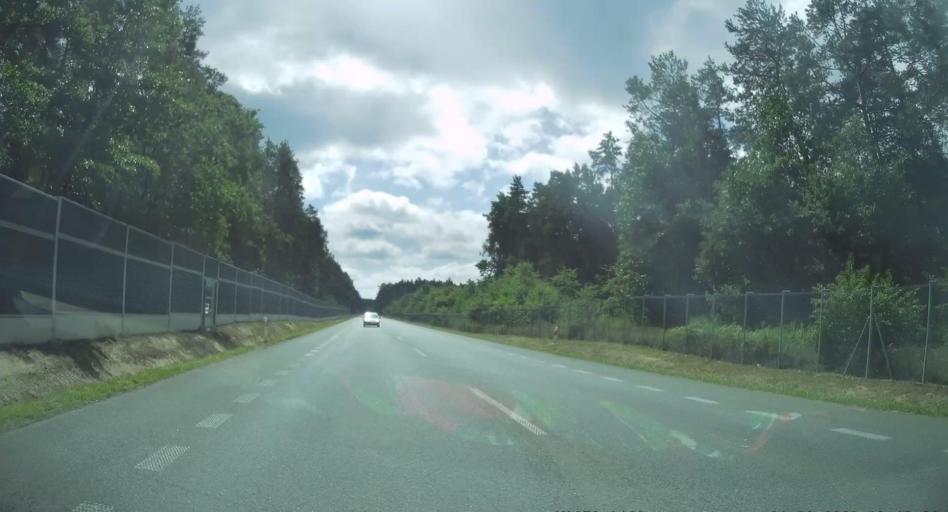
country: PL
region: Subcarpathian Voivodeship
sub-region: Powiat mielecki
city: Mielec
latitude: 50.2910
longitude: 21.4947
